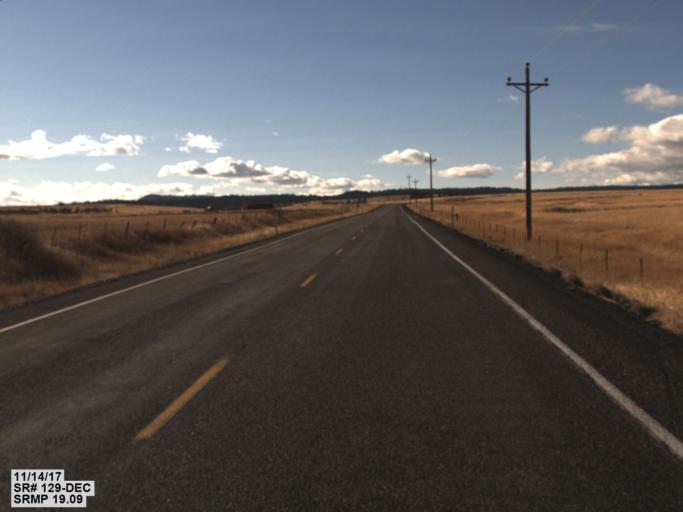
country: US
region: Washington
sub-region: Asotin County
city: Asotin
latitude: 46.1542
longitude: -117.1144
